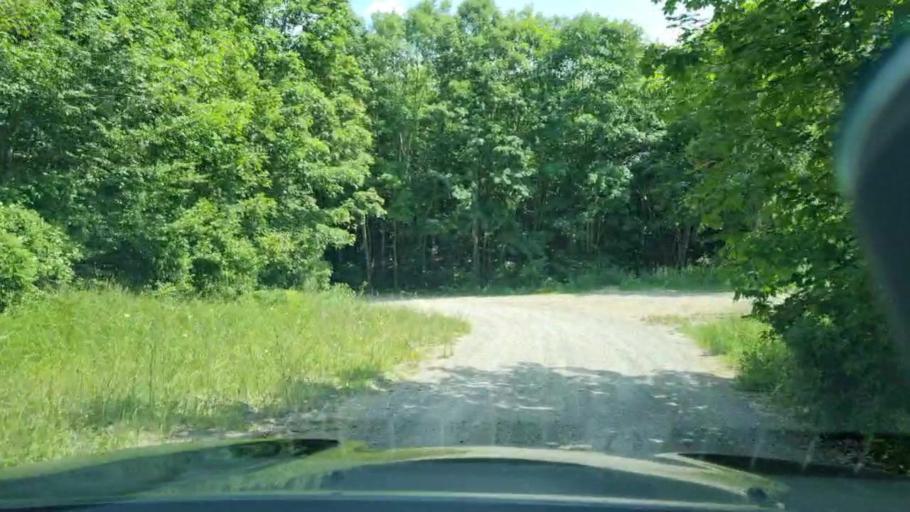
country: BA
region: Federation of Bosnia and Herzegovina
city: Bosansko Grahovo
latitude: 44.3263
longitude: 16.2331
